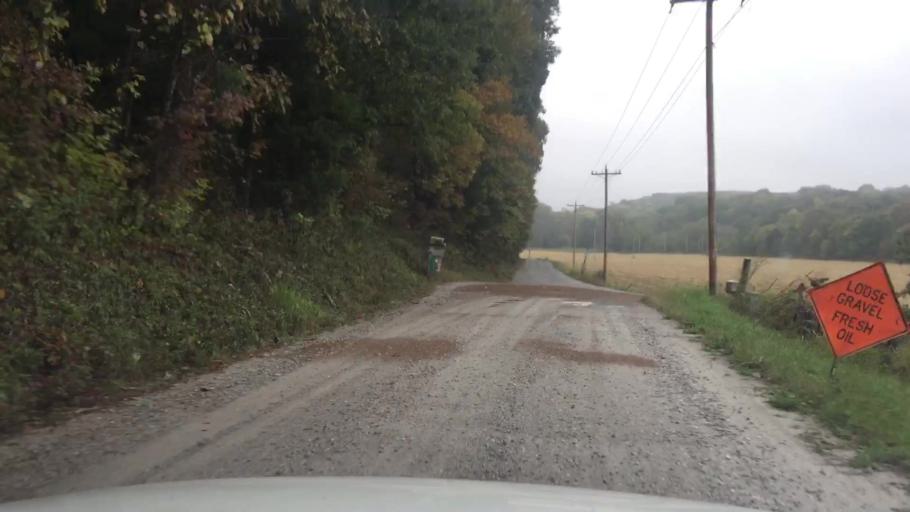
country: US
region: Missouri
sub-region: Boone County
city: Ashland
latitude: 38.8251
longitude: -92.3290
